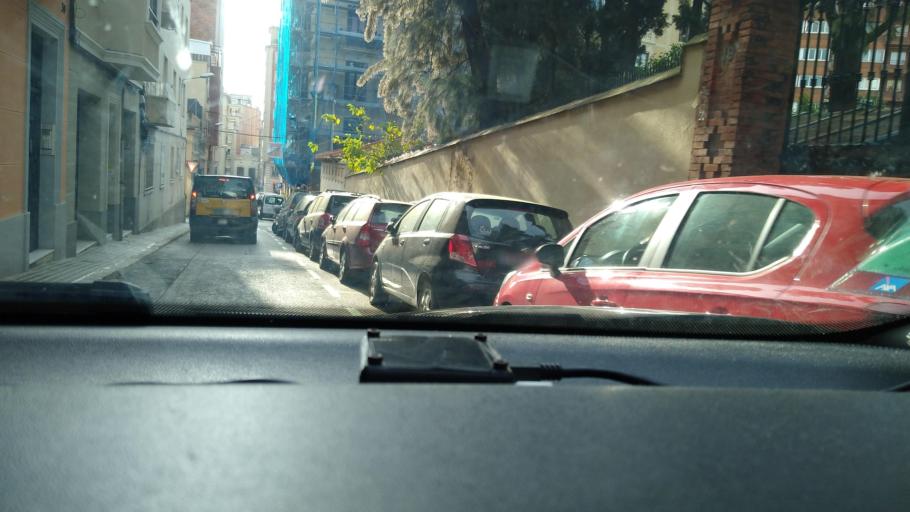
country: ES
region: Catalonia
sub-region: Provincia de Barcelona
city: Sarria-Sant Gervasi
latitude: 41.4064
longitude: 2.1458
